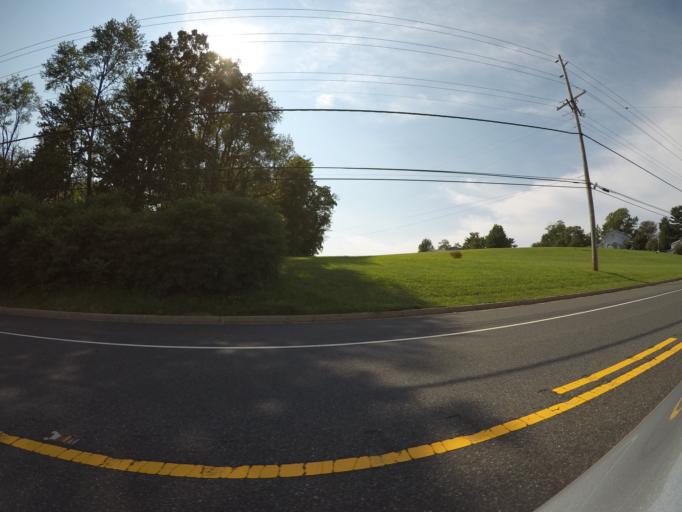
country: US
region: Maryland
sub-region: Harford County
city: Aberdeen
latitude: 39.5612
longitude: -76.1680
